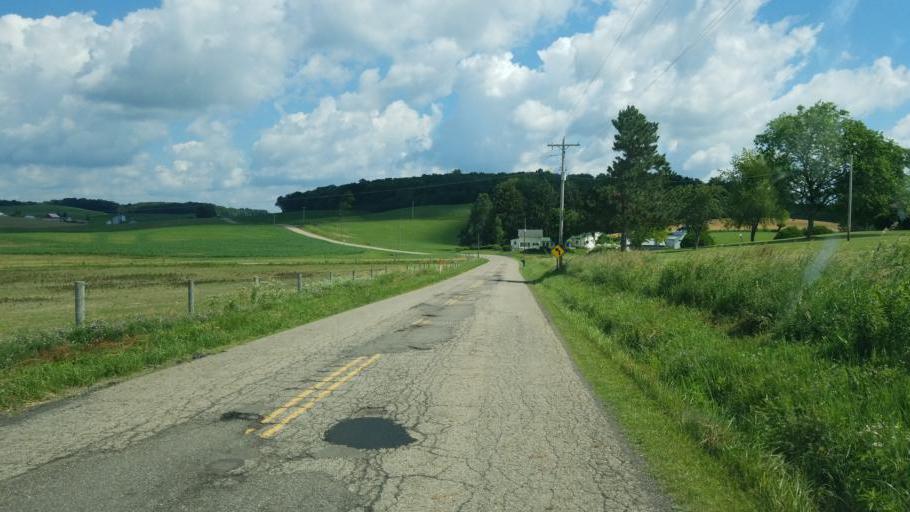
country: US
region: Ohio
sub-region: Knox County
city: Danville
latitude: 40.5086
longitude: -82.2588
